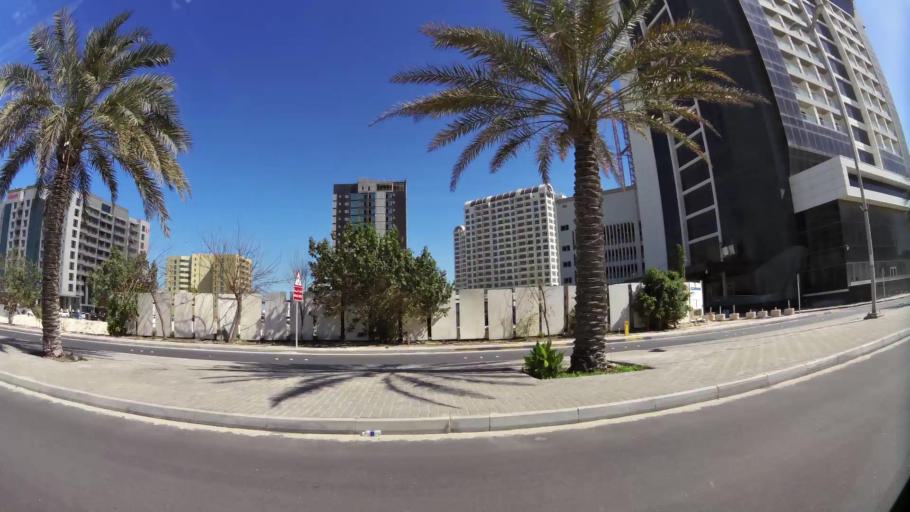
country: BH
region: Muharraq
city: Al Hadd
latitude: 26.2924
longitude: 50.6621
